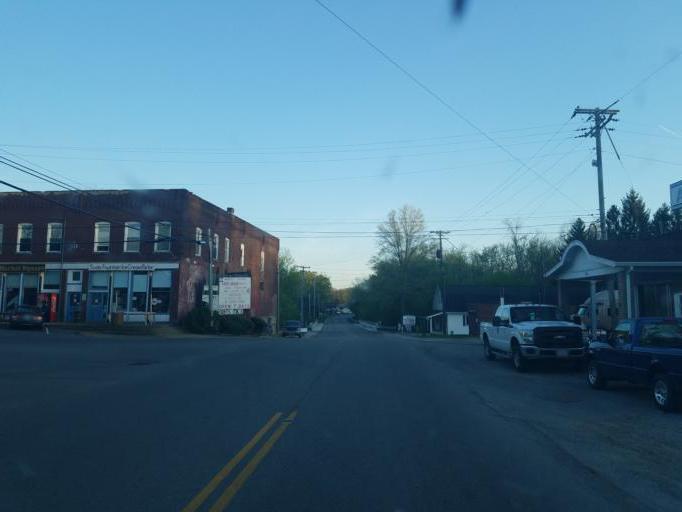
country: US
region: Ohio
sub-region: Ashtabula County
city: Andover
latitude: 41.4443
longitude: -80.5886
